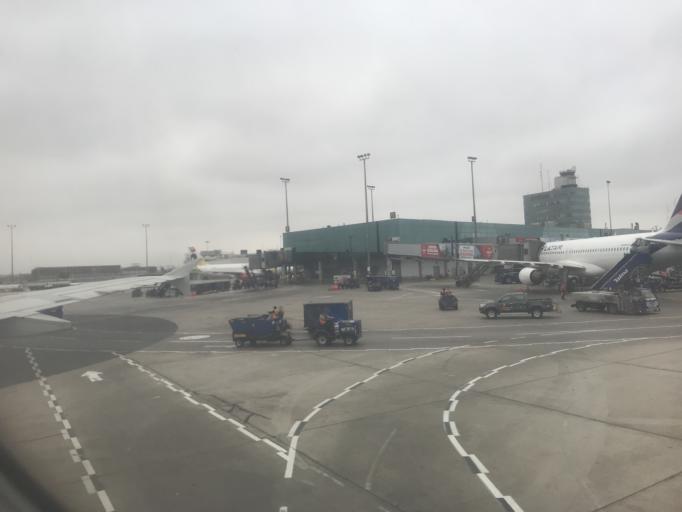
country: PE
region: Callao
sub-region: Callao
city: Callao
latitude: -12.0217
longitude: -77.1111
